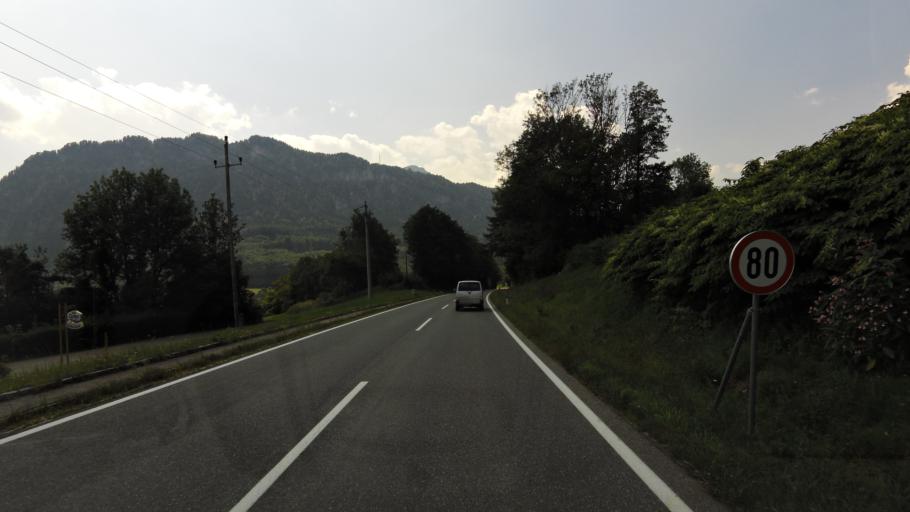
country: AT
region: Upper Austria
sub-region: Politischer Bezirk Vocklabruck
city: Steinbach am Attersee
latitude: 47.8068
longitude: 13.4869
